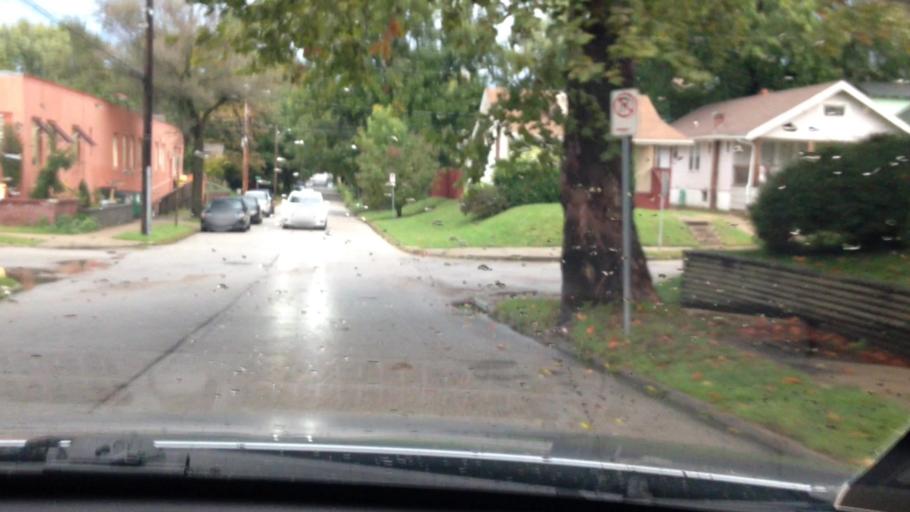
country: US
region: Kansas
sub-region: Johnson County
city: Mission Hills
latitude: 38.9938
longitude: -94.5918
